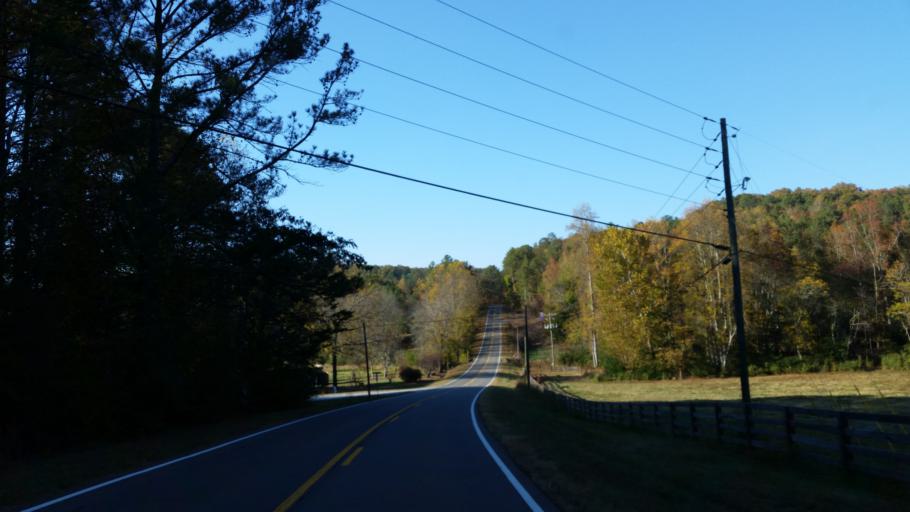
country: US
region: Georgia
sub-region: Pickens County
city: Jasper
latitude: 34.5279
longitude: -84.4770
